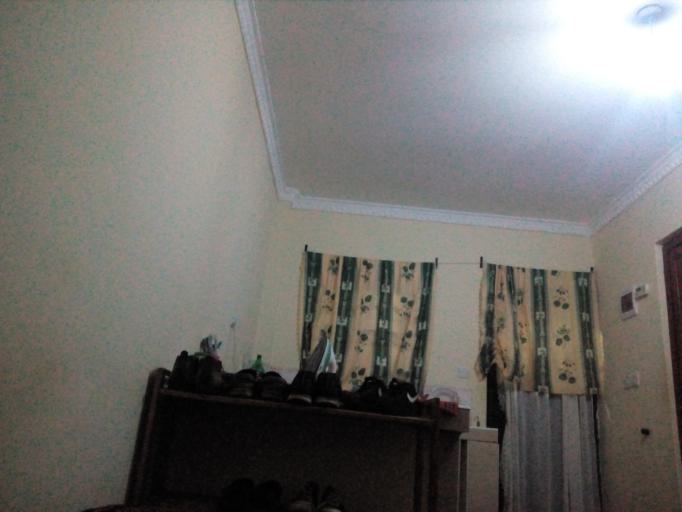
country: KE
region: Kirinyaga
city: Keruguya
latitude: -0.3931
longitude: 37.1348
